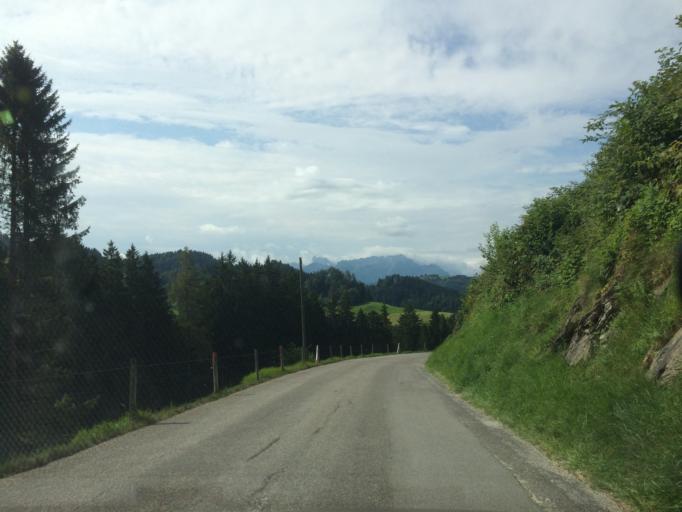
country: CH
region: Appenzell Ausserrhoden
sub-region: Bezirk Mittelland
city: Gais
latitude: 47.3854
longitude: 9.4495
